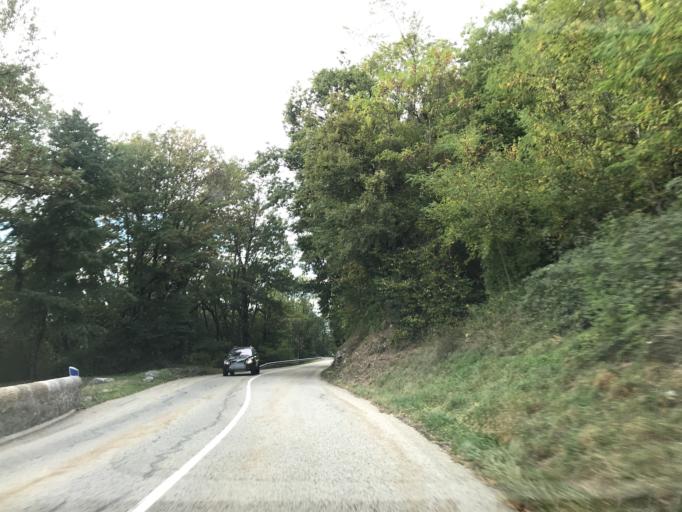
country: FR
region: Rhone-Alpes
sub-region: Departement de la Haute-Savoie
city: Menthon-Saint-Bernard
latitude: 45.8667
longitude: 6.1941
